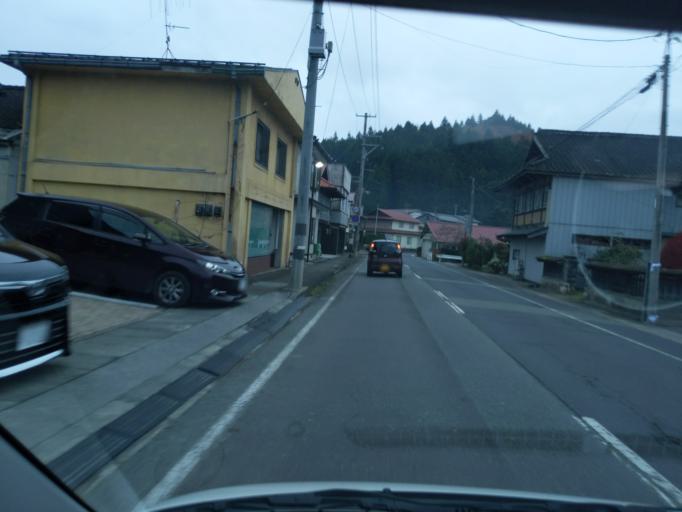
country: JP
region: Iwate
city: Mizusawa
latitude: 39.0457
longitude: 141.3665
